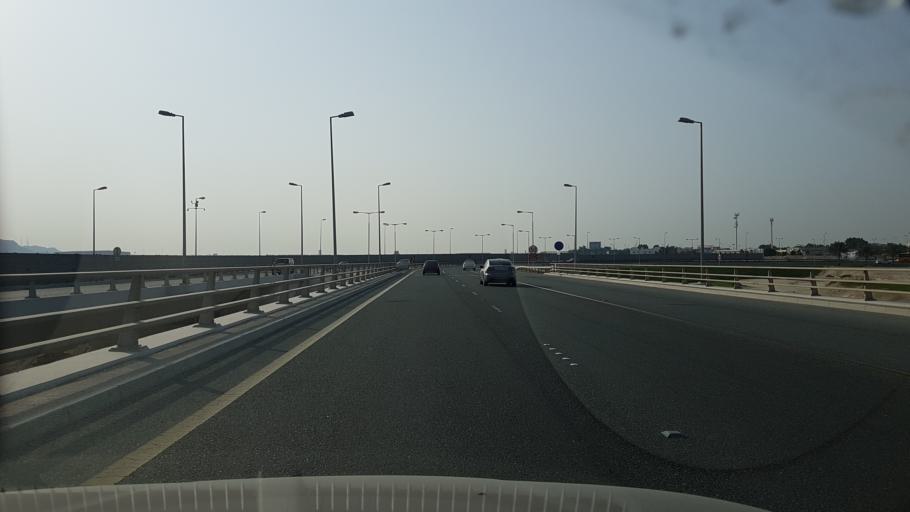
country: BH
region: Central Governorate
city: Dar Kulayb
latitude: 26.0587
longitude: 50.5182
